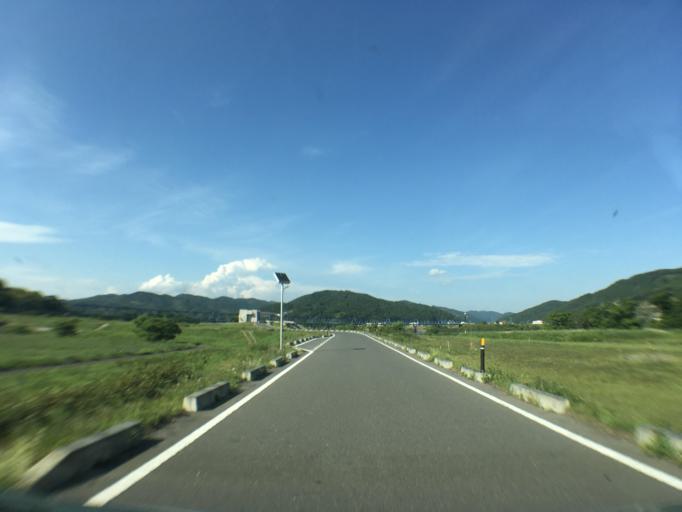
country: JP
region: Miyagi
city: Wakuya
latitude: 38.6052
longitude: 141.2926
